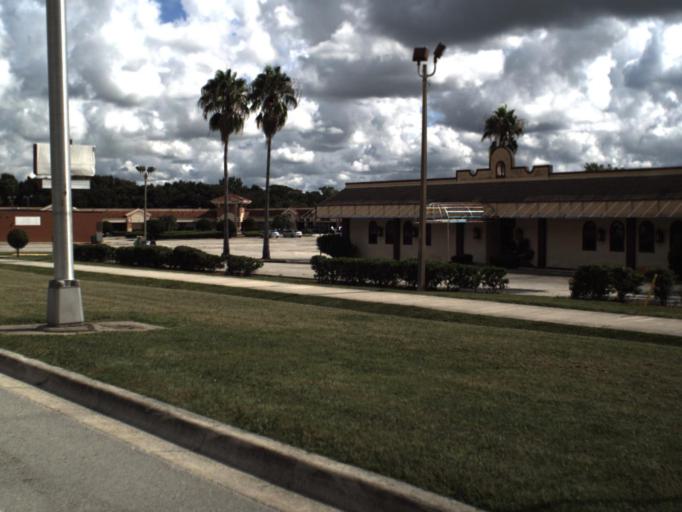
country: US
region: Florida
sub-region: Polk County
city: Gibsonia
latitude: 28.1079
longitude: -81.9735
